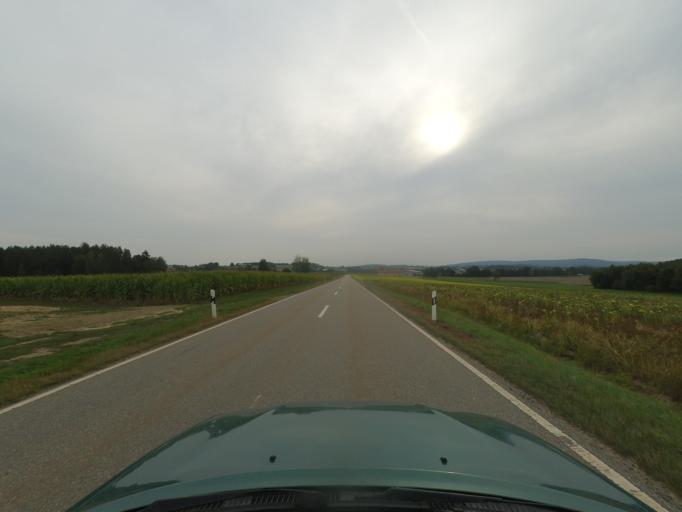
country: DE
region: Bavaria
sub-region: Upper Palatinate
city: Eslarn
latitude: 49.5863
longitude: 12.4928
